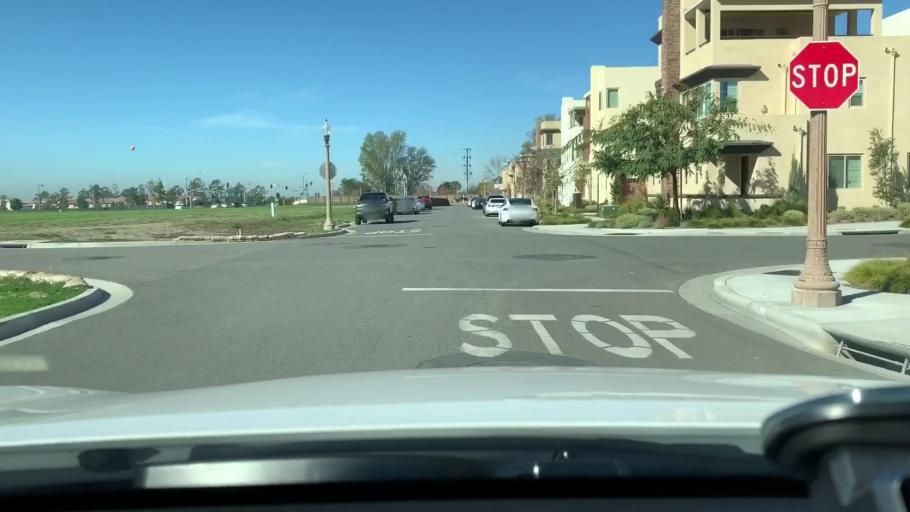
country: US
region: California
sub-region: Orange County
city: Lake Forest
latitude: 33.6810
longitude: -117.7391
